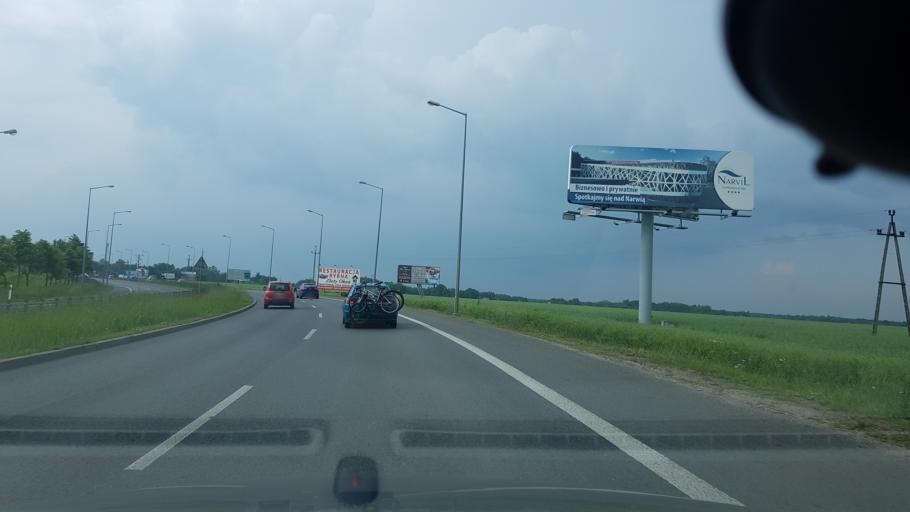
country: PL
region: Masovian Voivodeship
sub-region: Powiat legionowski
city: Bialobrzegi
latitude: 52.4668
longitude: 21.0298
